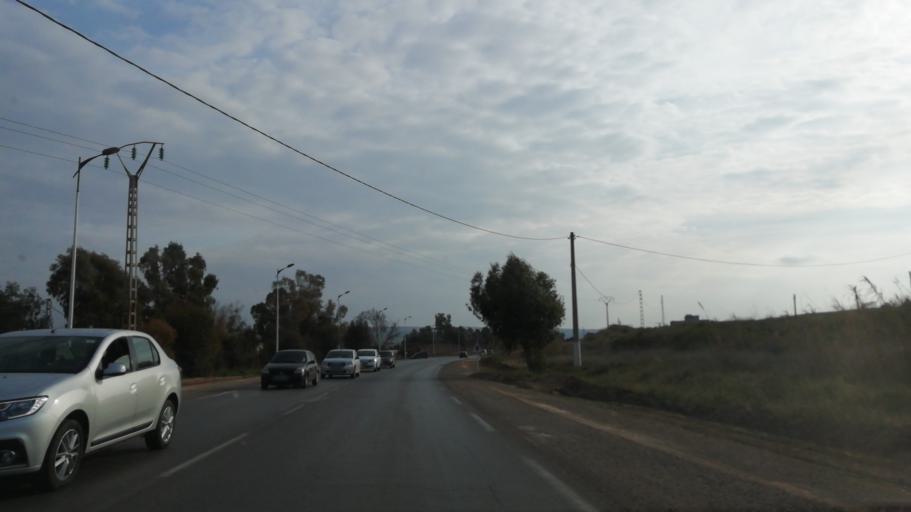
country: DZ
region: Mostaganem
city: Mostaganem
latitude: 35.8803
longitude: 0.0787
